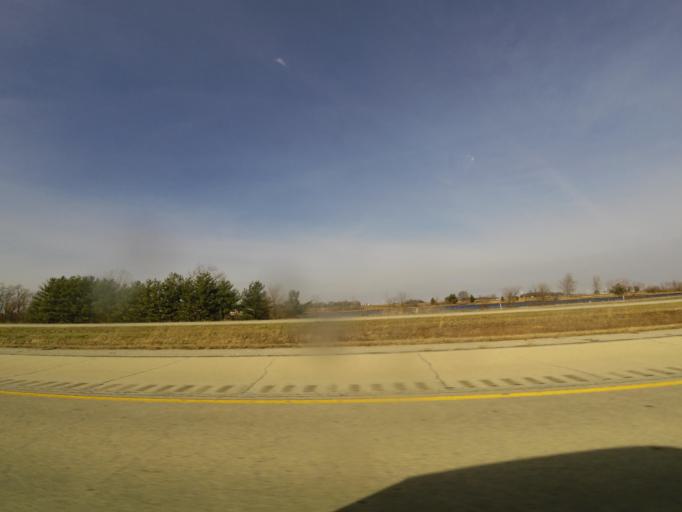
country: US
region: Illinois
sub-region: Macon County
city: Forsyth
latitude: 39.8990
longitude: -89.0003
